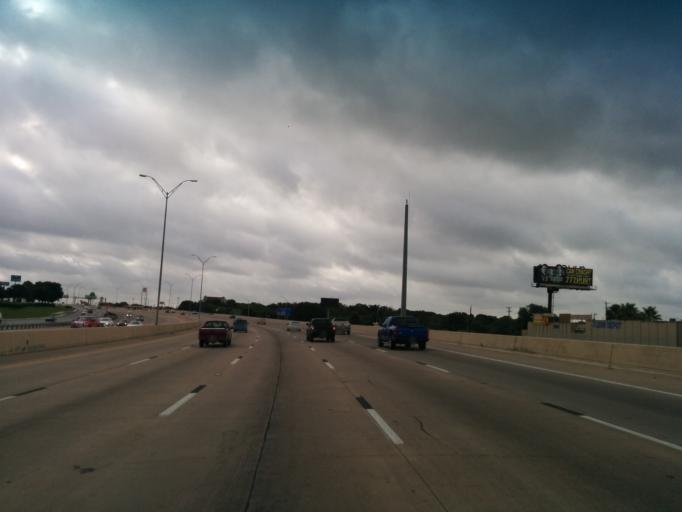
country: US
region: Texas
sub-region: Bexar County
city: Balcones Heights
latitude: 29.4858
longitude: -98.5421
